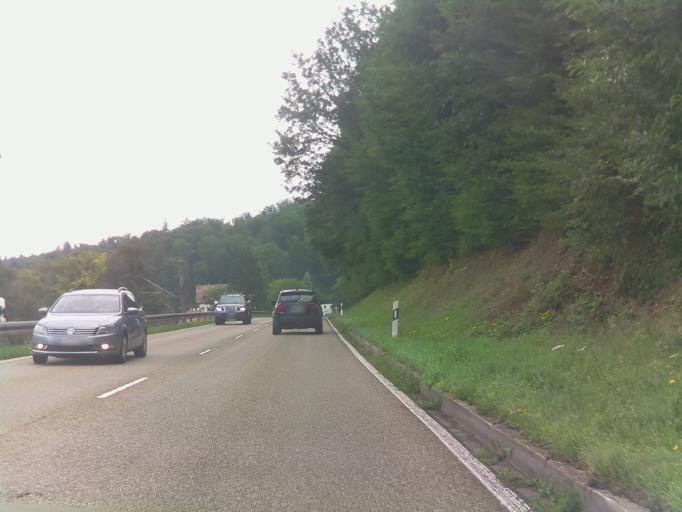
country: DE
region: Baden-Wuerttemberg
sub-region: Karlsruhe Region
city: Ettlingen
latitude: 48.9112
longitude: 8.4549
